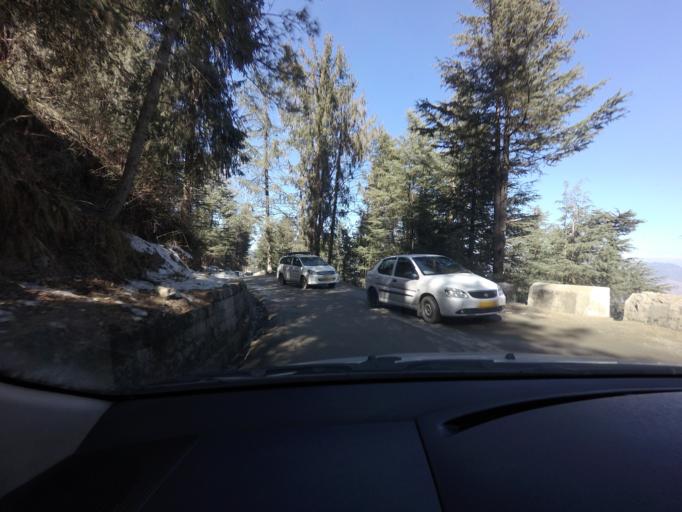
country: IN
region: Himachal Pradesh
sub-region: Shimla
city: Theog
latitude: 31.1000
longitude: 77.2666
